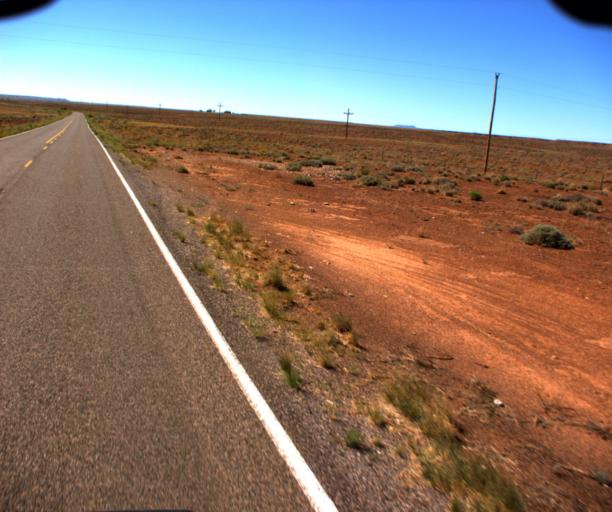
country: US
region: Arizona
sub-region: Coconino County
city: LeChee
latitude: 35.1811
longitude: -110.9296
